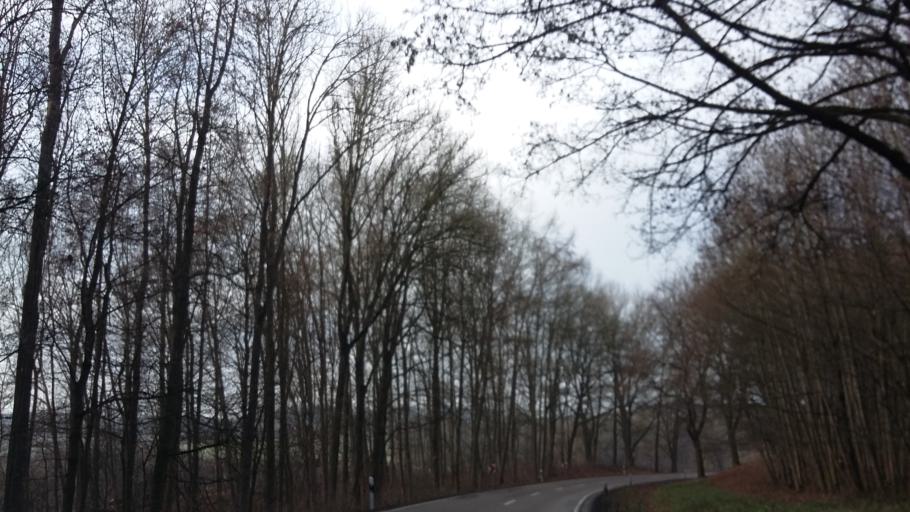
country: DE
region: Bavaria
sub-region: Swabia
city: Sielenbach
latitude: 48.4193
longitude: 11.1557
